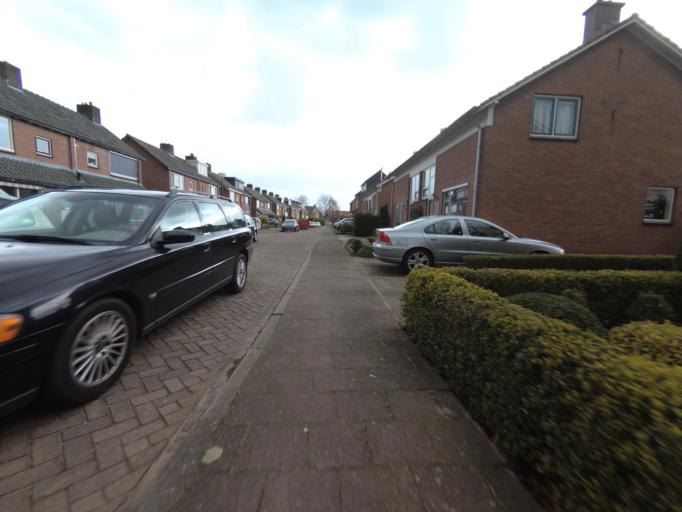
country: NL
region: Gelderland
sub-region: Gemeente Barneveld
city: Terschuur
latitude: 52.1394
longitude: 5.4933
